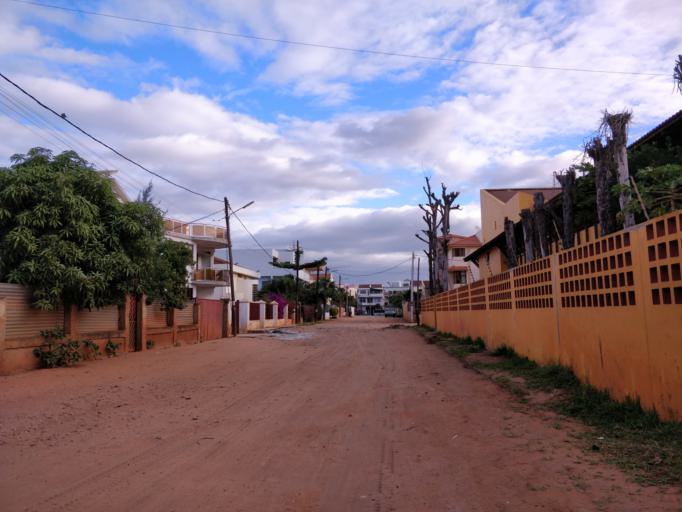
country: MZ
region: Maputo City
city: Maputo
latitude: -25.9457
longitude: 32.6167
